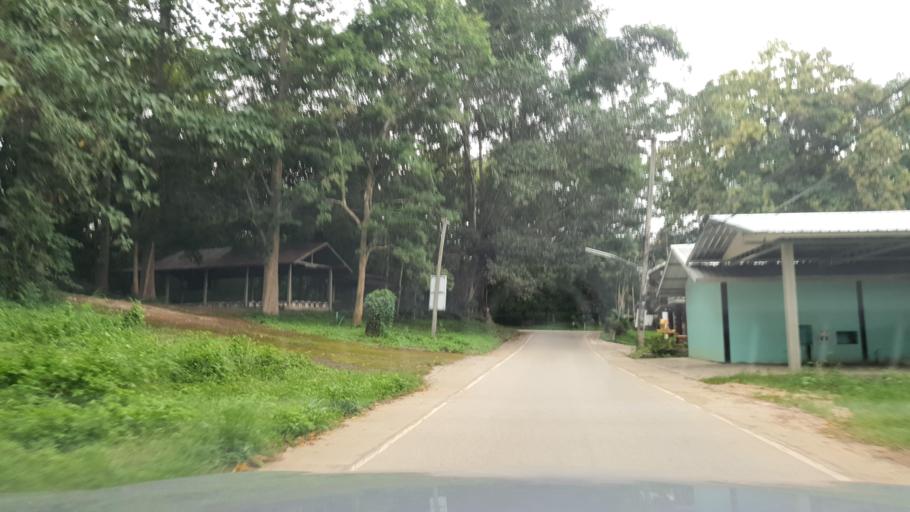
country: TH
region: Chiang Mai
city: Chiang Mai
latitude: 18.9271
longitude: 98.9101
